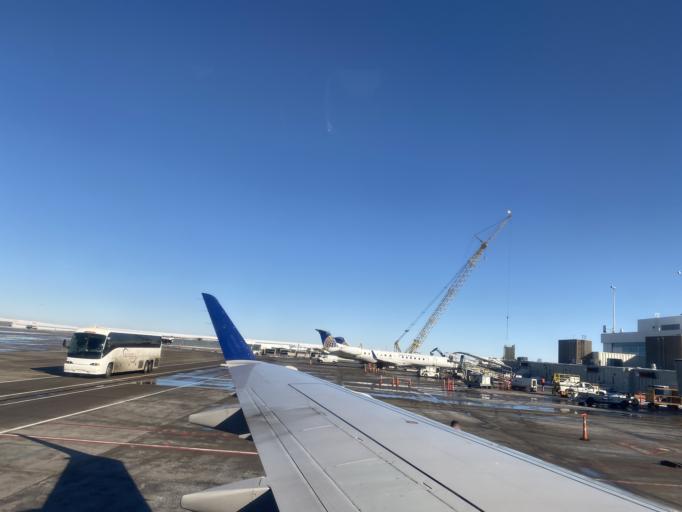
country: US
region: Colorado
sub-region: Weld County
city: Lochbuie
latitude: 39.8595
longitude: -104.6696
